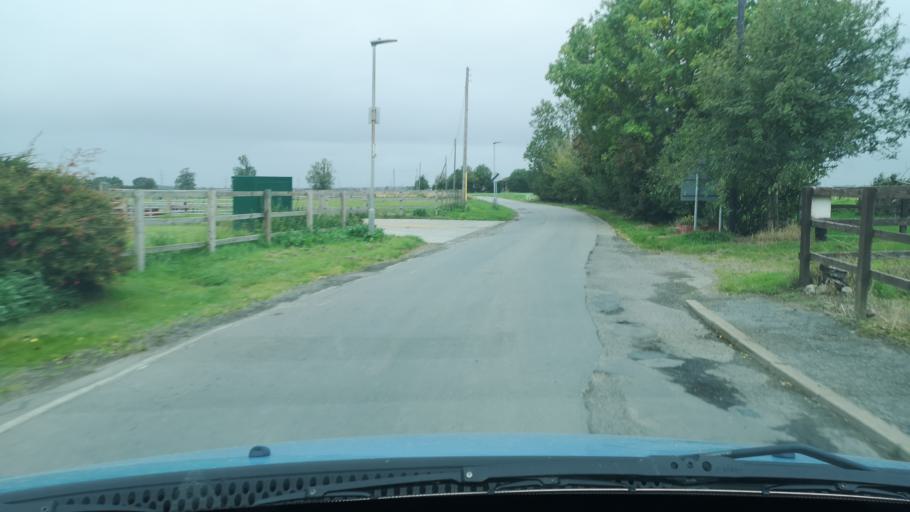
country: GB
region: England
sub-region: North Lincolnshire
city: Burton upon Stather
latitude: 53.6632
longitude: -0.7185
